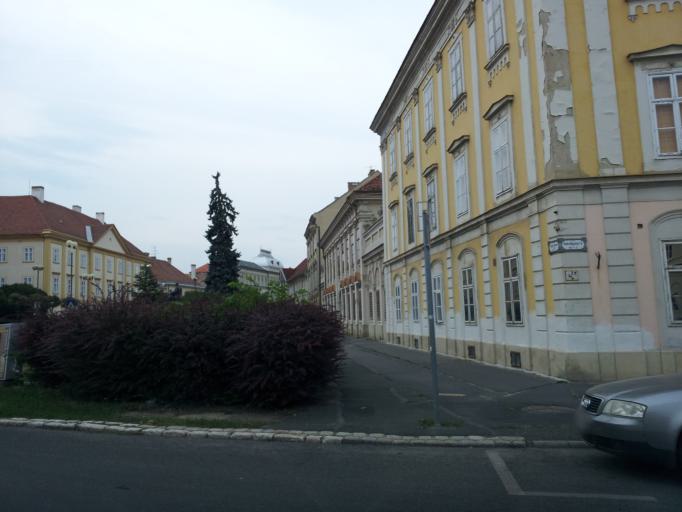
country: HU
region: Vas
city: Szombathely
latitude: 47.2312
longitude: 16.6190
